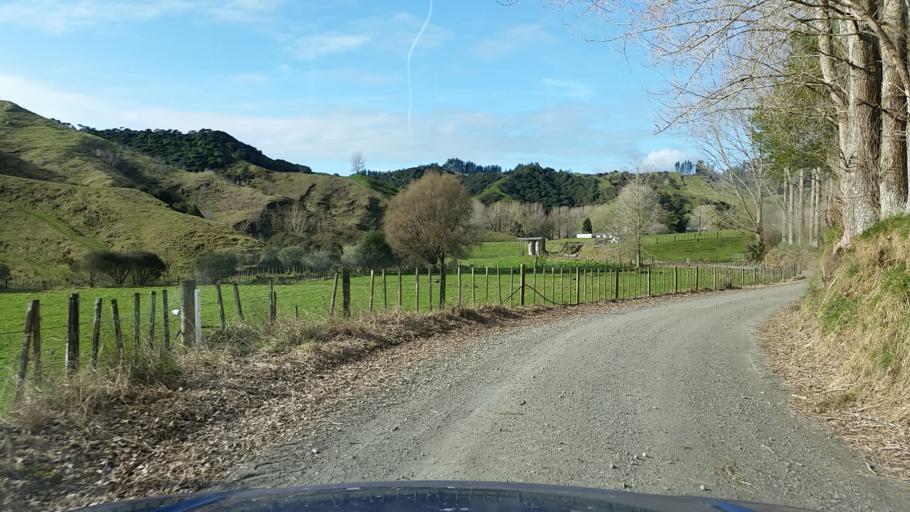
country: NZ
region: Taranaki
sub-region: South Taranaki District
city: Eltham
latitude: -39.2603
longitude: 174.5847
